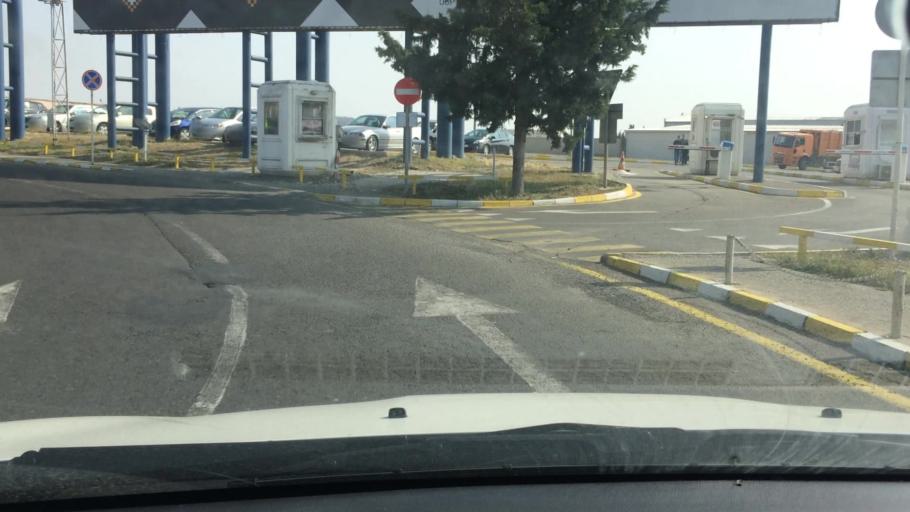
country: GE
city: Didi Lilo
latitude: 41.6692
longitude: 44.9659
